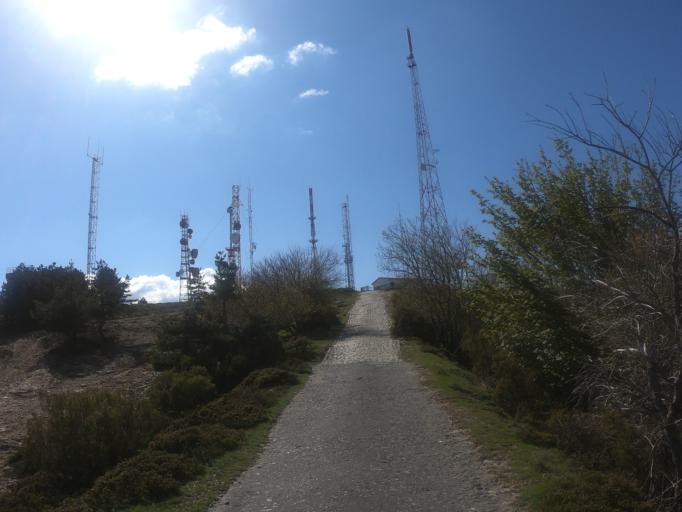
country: PT
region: Vila Real
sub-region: Mesao Frio
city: Mesao Frio
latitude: 41.2479
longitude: -7.8837
